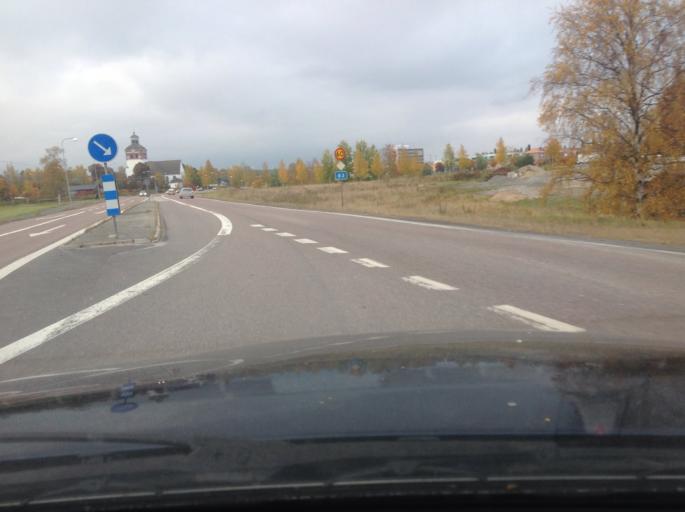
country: SE
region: Gaevleborg
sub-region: Bollnas Kommun
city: Bollnas
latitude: 61.3413
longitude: 16.3929
